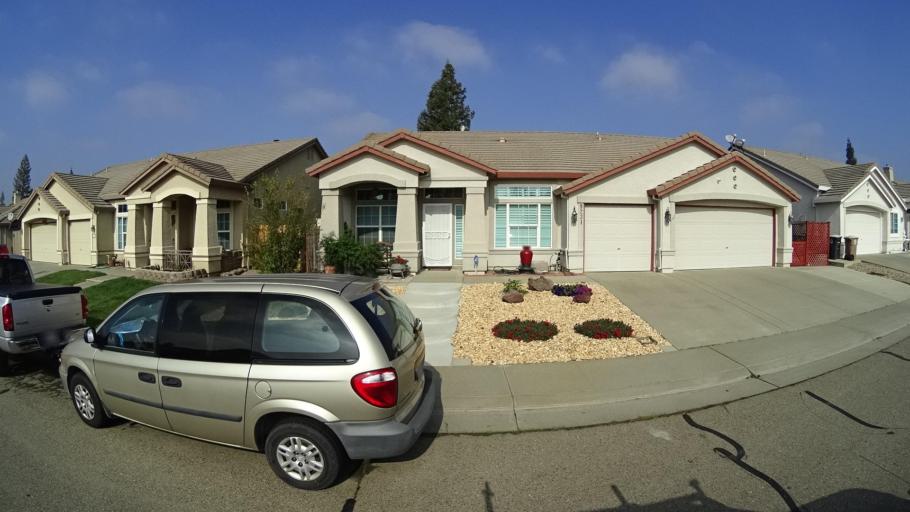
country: US
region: California
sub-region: Sacramento County
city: Vineyard
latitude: 38.4501
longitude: -121.3560
